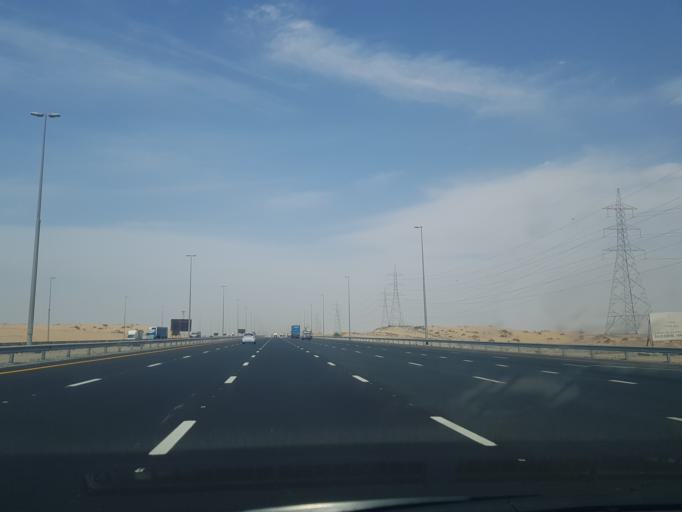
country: AE
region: Ash Shariqah
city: Sharjah
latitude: 25.2477
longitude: 55.5709
